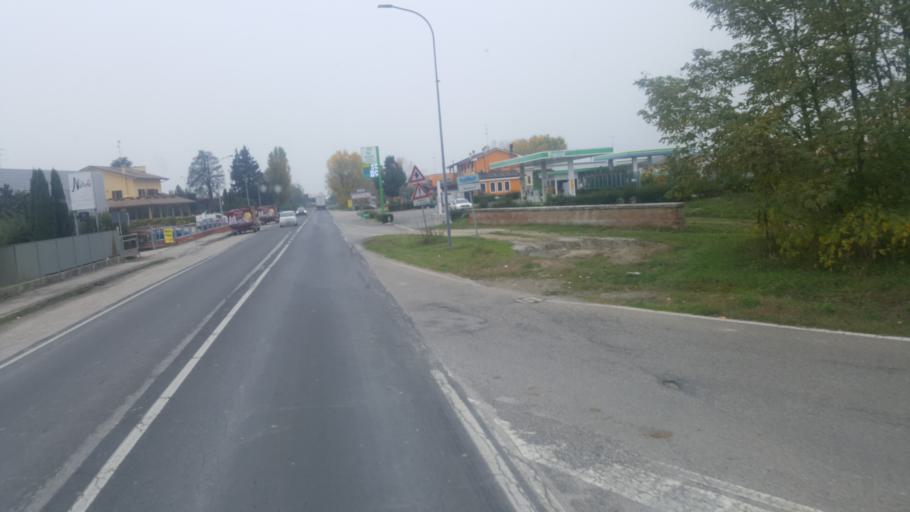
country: IT
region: Emilia-Romagna
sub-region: Provincia di Ferrara
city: Bondeno
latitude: 44.8997
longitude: 11.4050
